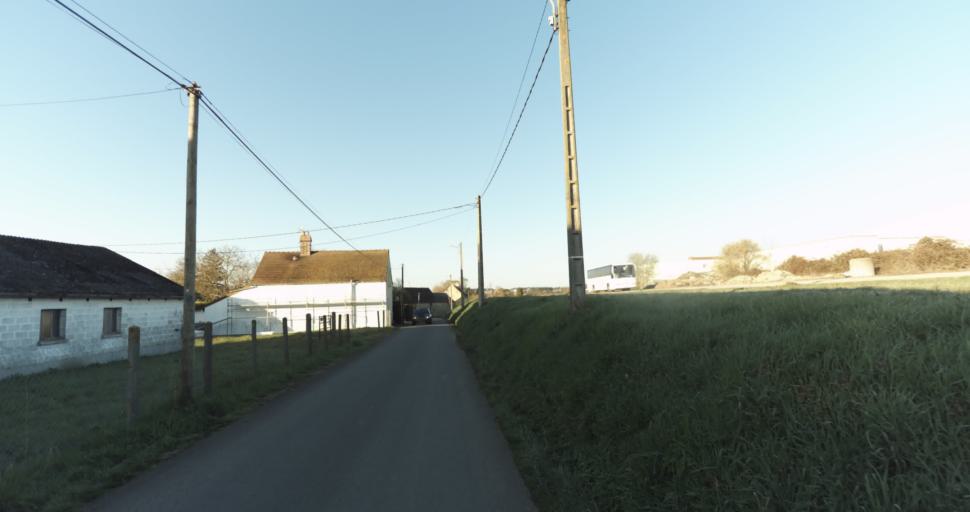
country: FR
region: Lower Normandy
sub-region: Departement du Calvados
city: Saint-Pierre-sur-Dives
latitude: 49.0221
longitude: -0.0414
